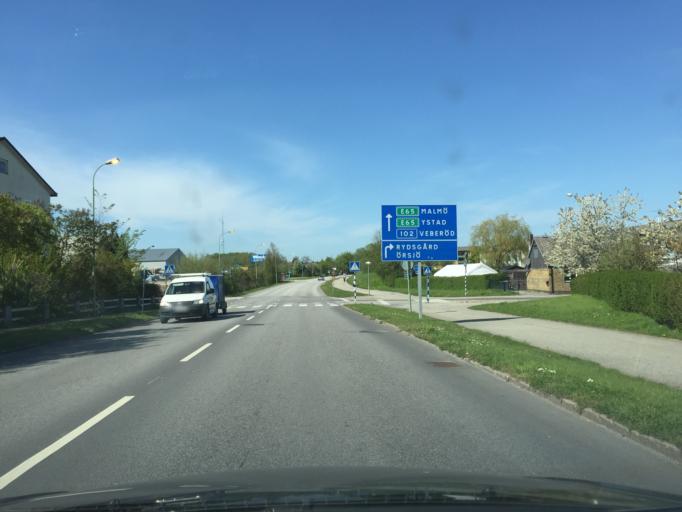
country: SE
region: Skane
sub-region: Skurups Kommun
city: Skurup
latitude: 55.4815
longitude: 13.5029
